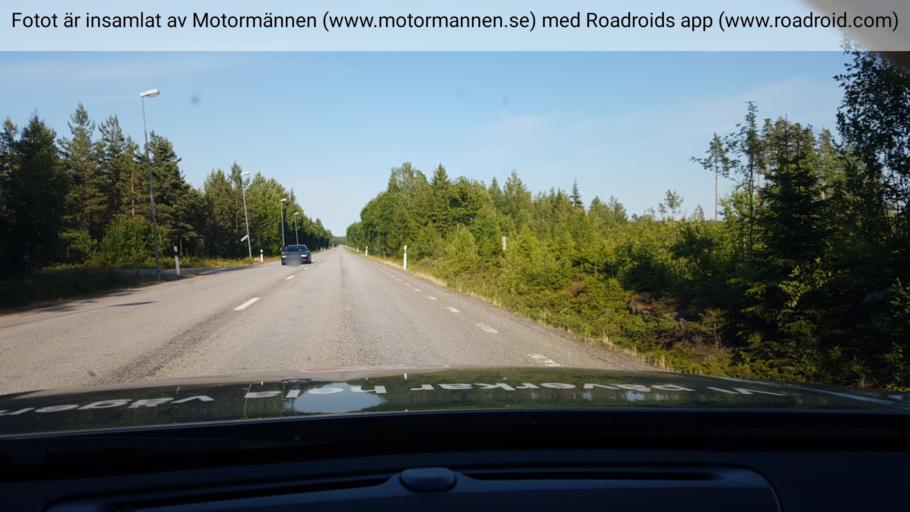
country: SE
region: Uppsala
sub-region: Osthammars Kommun
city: Gimo
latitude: 60.1651
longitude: 18.1554
